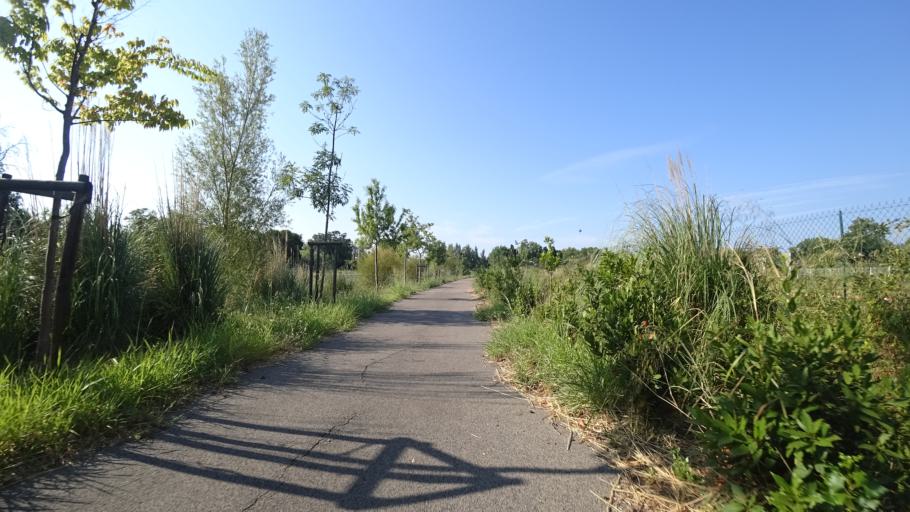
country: FR
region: Languedoc-Roussillon
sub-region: Departement des Pyrenees-Orientales
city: Perpignan
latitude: 42.7185
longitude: 2.9033
